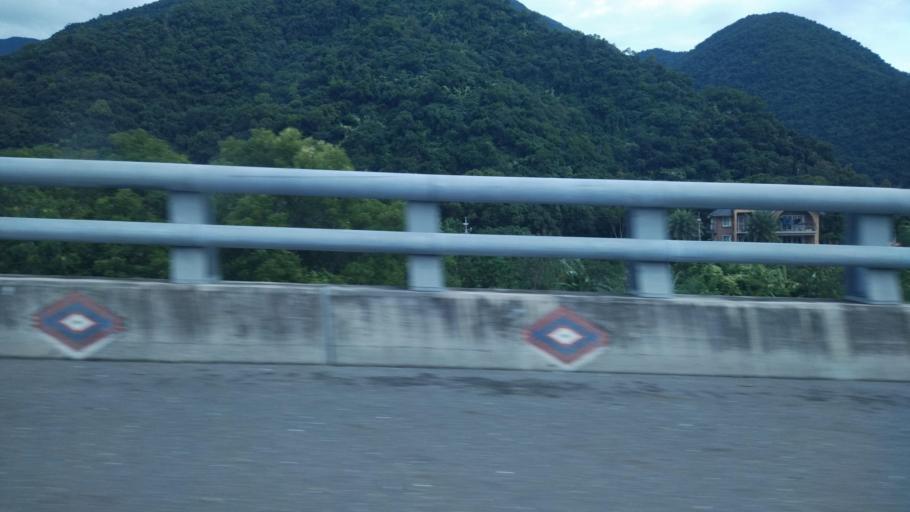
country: TW
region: Taiwan
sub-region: Yilan
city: Yilan
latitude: 24.4647
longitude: 121.7946
